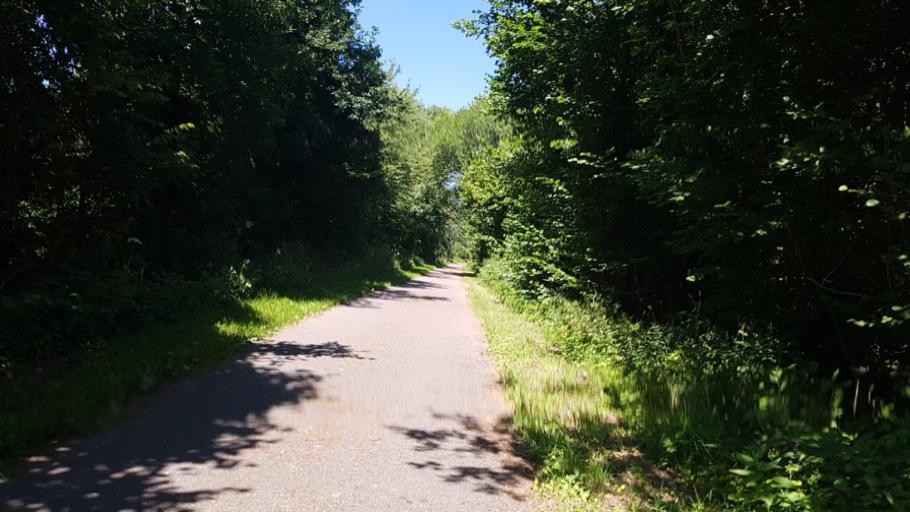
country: BE
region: Wallonia
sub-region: Province du Hainaut
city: Beaumont
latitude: 50.2312
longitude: 4.2436
